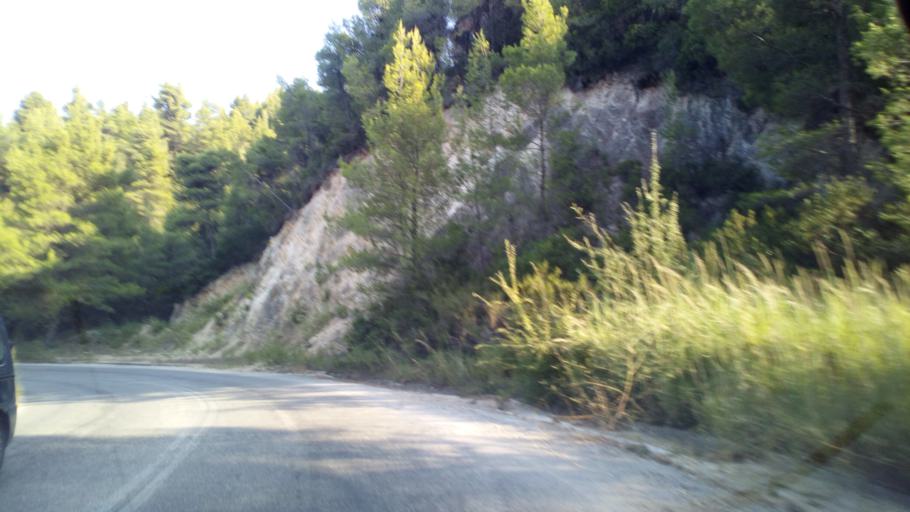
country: GR
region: Central Macedonia
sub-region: Nomos Chalkidikis
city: Neos Marmaras
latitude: 40.1722
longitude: 23.8449
